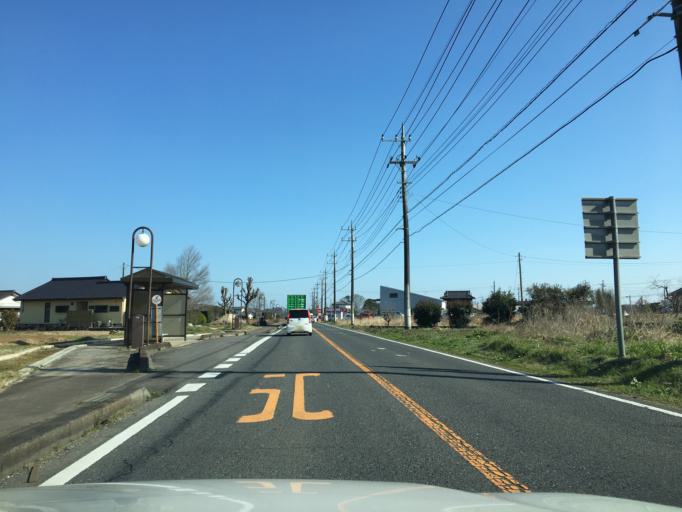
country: JP
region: Ibaraki
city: Omiya
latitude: 36.5388
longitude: 140.3415
